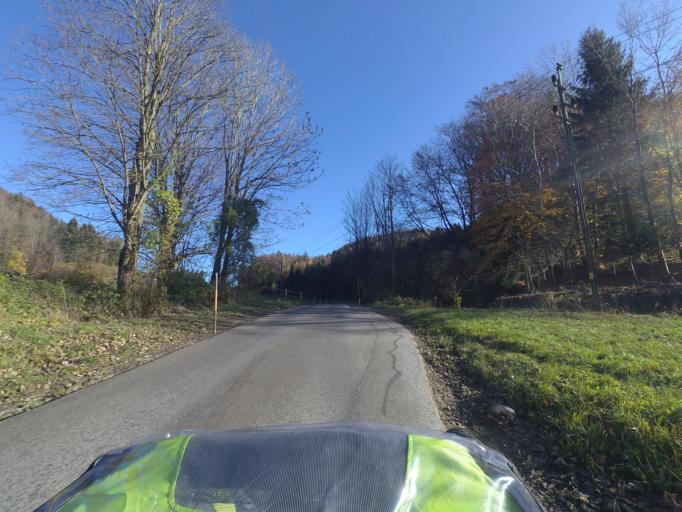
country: AT
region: Salzburg
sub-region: Politischer Bezirk Hallein
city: Puch bei Hallein
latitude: 47.7291
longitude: 13.1125
